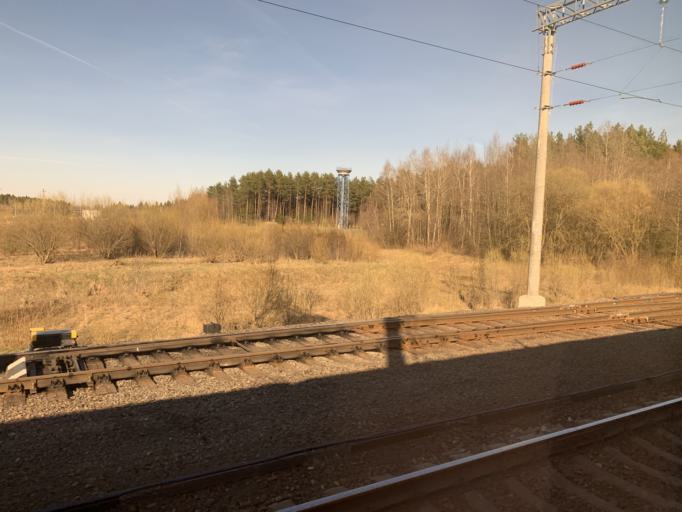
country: BY
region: Grodnenskaya
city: Astravyets
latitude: 54.5891
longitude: 25.9104
